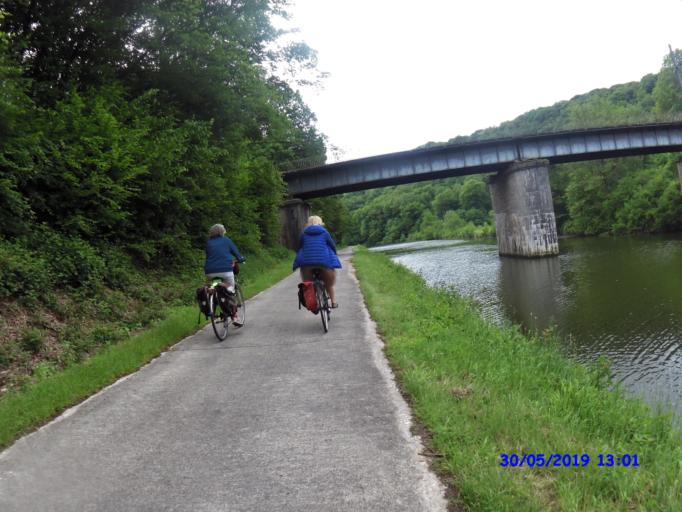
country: BE
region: Wallonia
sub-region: Province du Hainaut
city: Thuin
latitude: 50.3465
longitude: 4.3010
